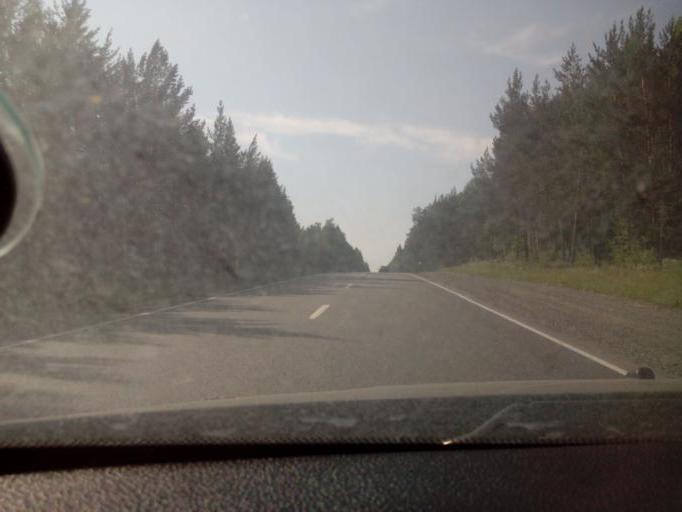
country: RU
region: Sverdlovsk
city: Iset'
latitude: 57.1083
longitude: 60.3453
